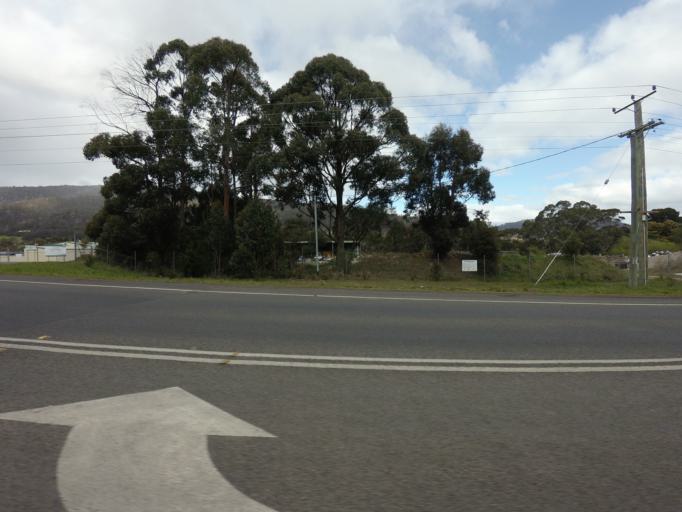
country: AU
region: Tasmania
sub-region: Huon Valley
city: Huonville
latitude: -43.0521
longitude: 147.0369
